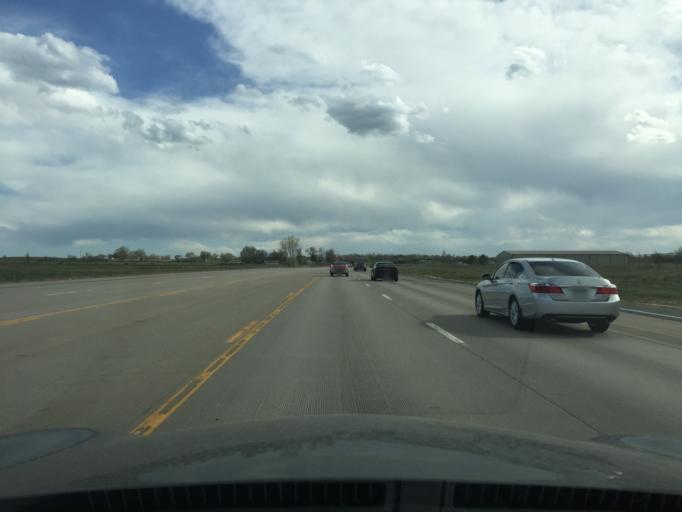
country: US
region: Colorado
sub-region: Boulder County
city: Lafayette
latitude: 40.0426
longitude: -105.1027
